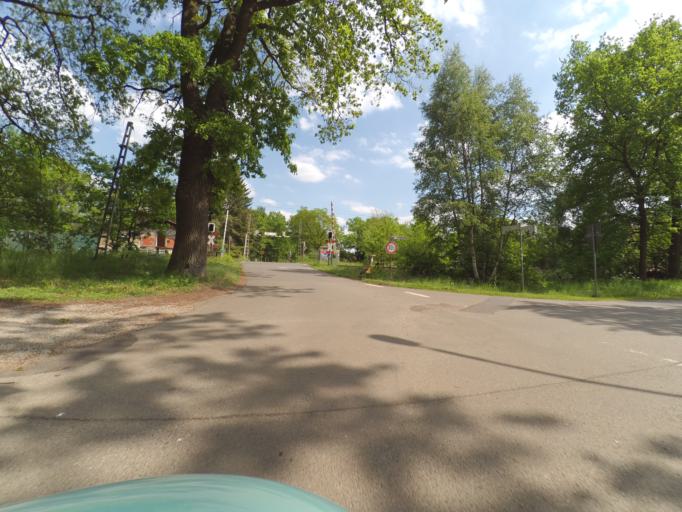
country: DE
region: Lower Saxony
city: Adelheidsdorf
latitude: 52.5440
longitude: 10.0362
